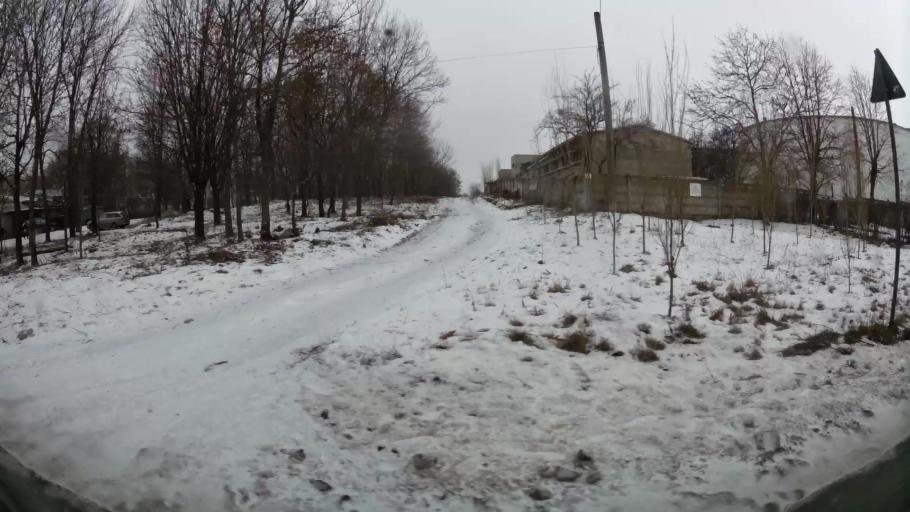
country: RO
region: Prahova
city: Ploiesti
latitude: 44.9641
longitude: 26.0062
